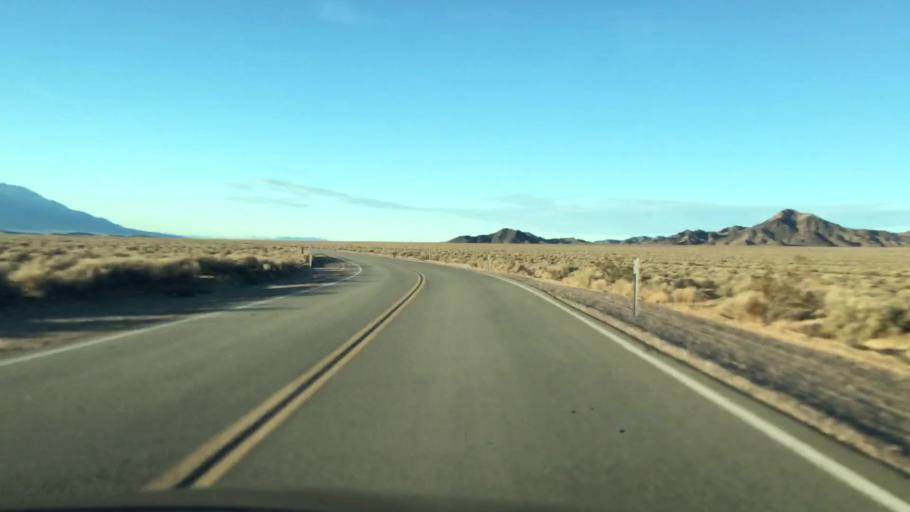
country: US
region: California
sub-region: San Bernardino County
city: Fort Irwin
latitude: 35.3440
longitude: -116.0838
